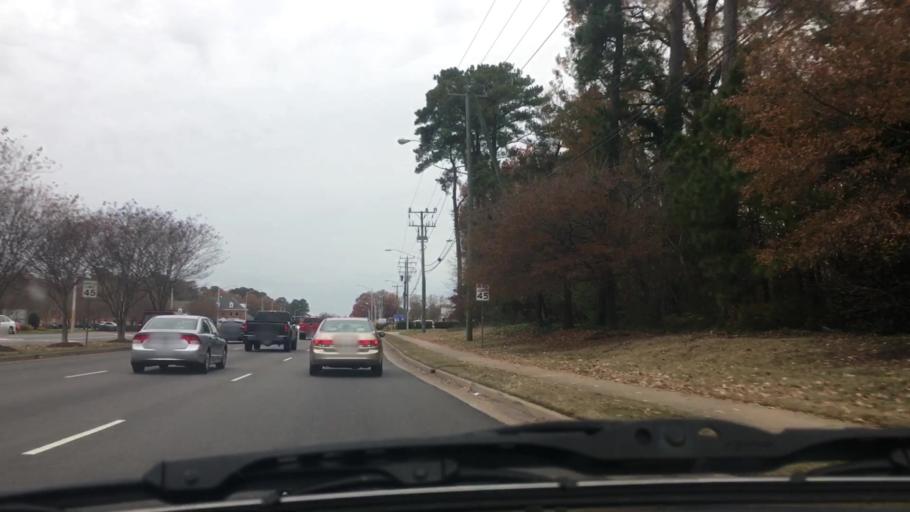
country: US
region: Virginia
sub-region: City of Chesapeake
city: Chesapeake
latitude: 36.8238
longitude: -76.1269
